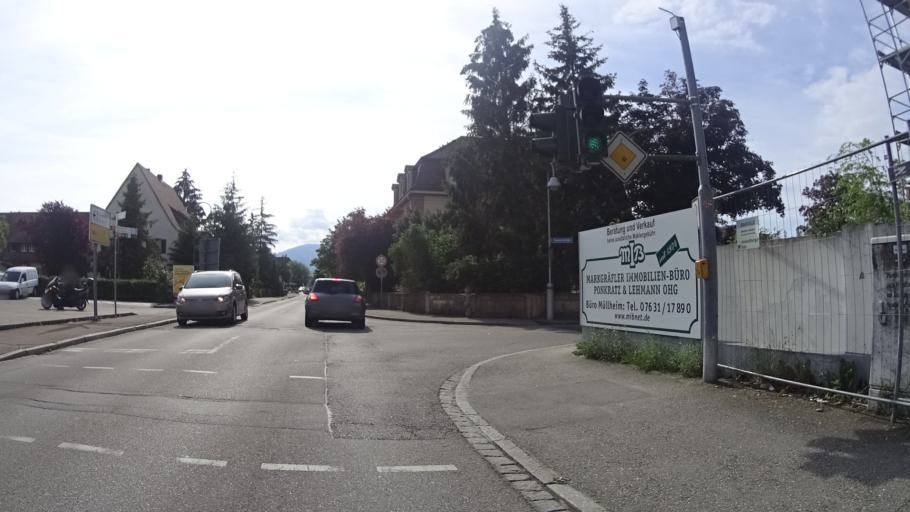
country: DE
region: Baden-Wuerttemberg
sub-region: Freiburg Region
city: Neuenburg am Rhein
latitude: 47.8126
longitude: 7.5663
